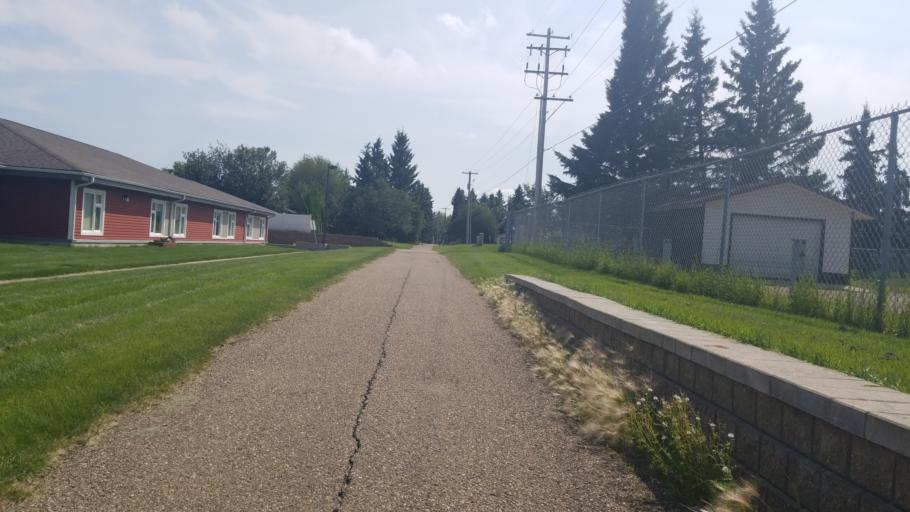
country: CA
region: Saskatchewan
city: Lloydminster
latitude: 53.2740
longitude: -110.0176
